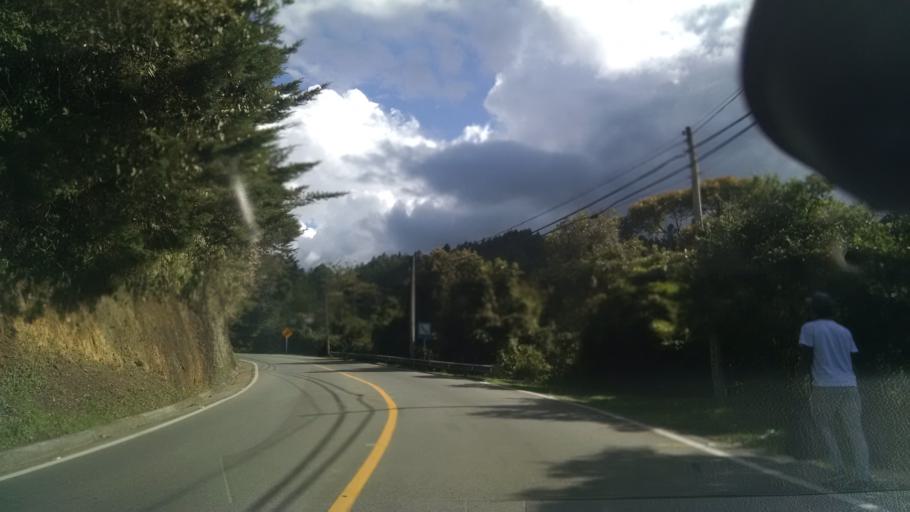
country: CO
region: Antioquia
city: El Retiro
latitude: 6.0878
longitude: -75.4790
